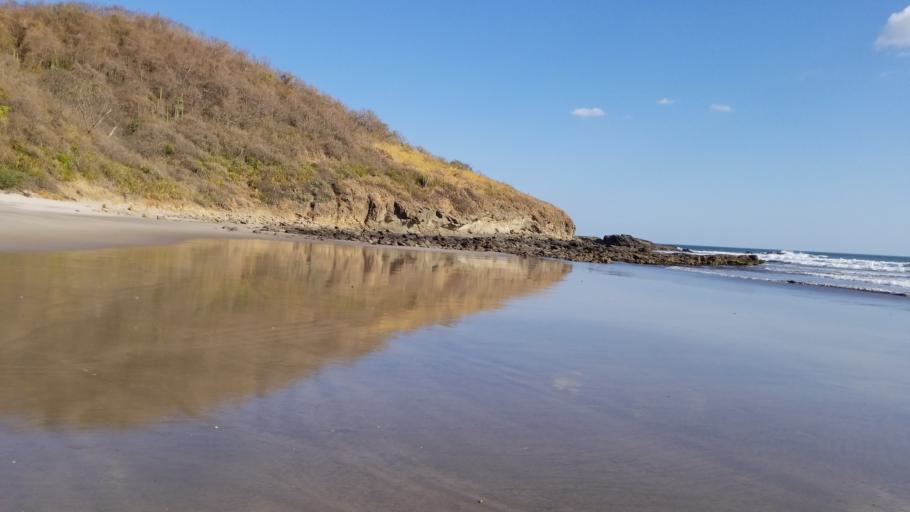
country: NI
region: Rivas
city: Tola
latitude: 11.4794
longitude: -86.1485
